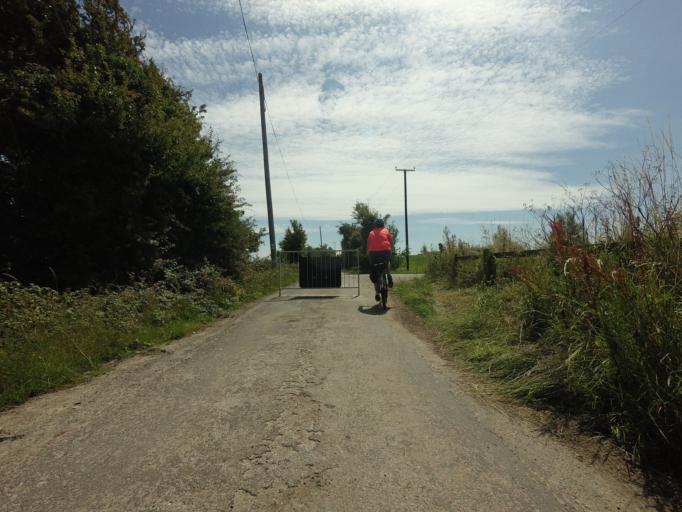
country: GB
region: England
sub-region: Kent
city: Stone
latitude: 50.9920
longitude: 0.8336
